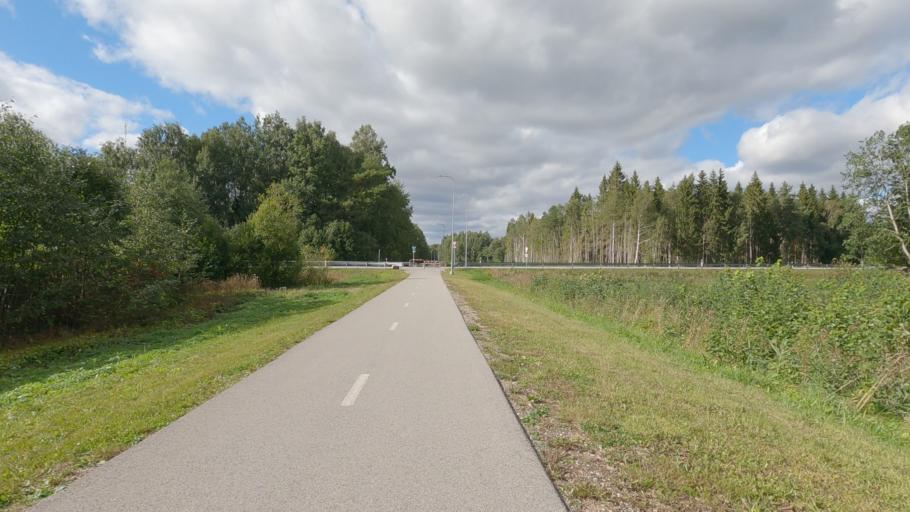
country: EE
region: Raplamaa
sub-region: Rapla vald
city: Rapla
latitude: 59.0175
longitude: 24.7814
